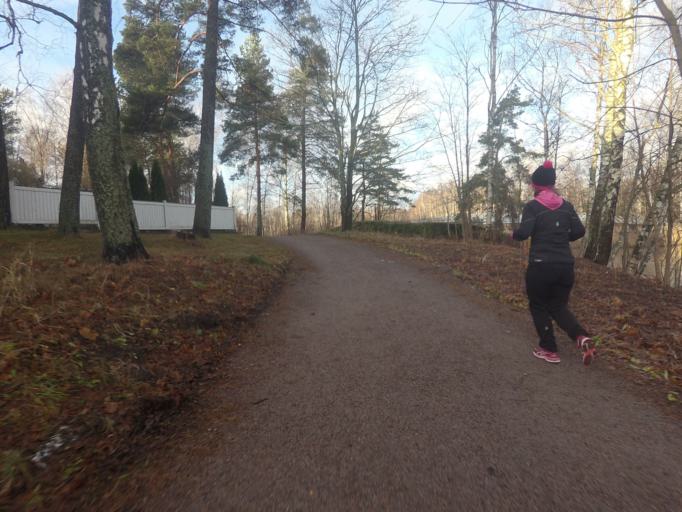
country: FI
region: Uusimaa
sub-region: Helsinki
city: Koukkuniemi
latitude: 60.1569
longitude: 24.7671
